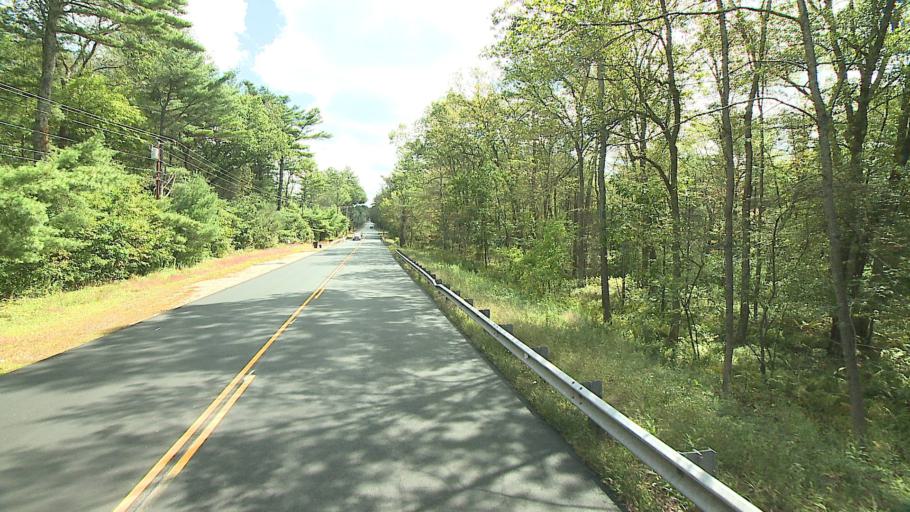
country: US
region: Connecticut
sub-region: Windham County
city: Thompson
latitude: 41.9174
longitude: -71.8153
